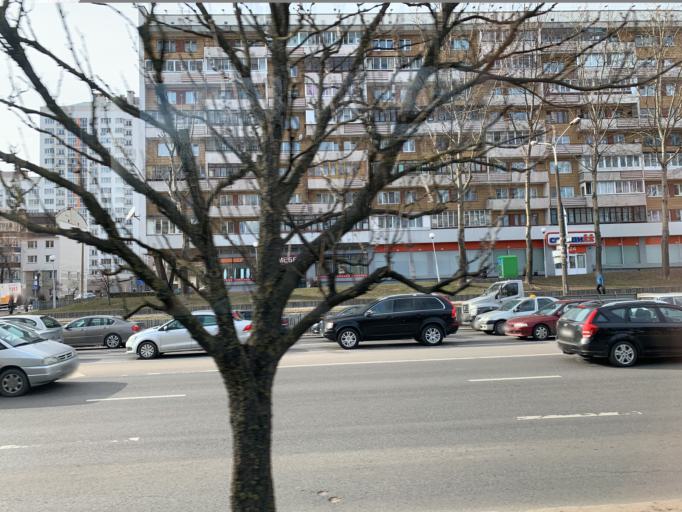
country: BY
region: Minsk
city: Bal'shavik
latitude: 53.9523
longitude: 27.6184
